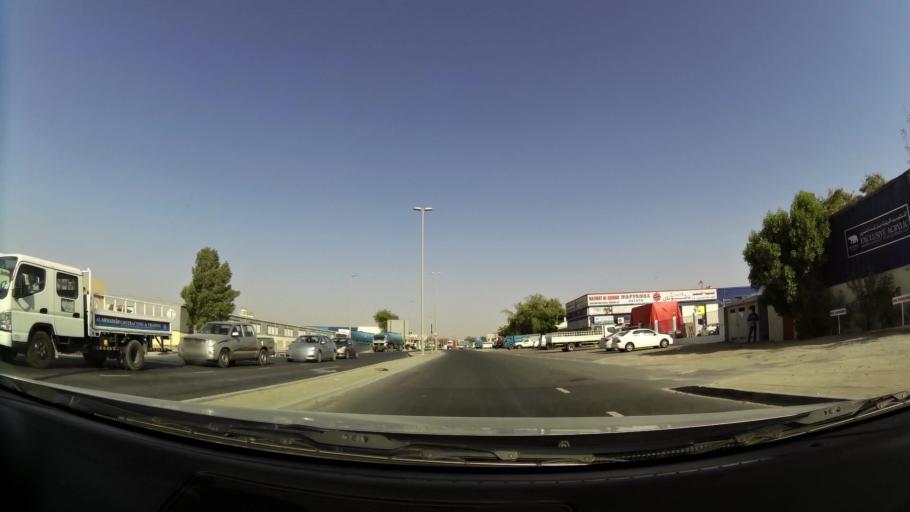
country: AE
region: Dubai
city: Dubai
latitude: 25.1202
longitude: 55.2255
